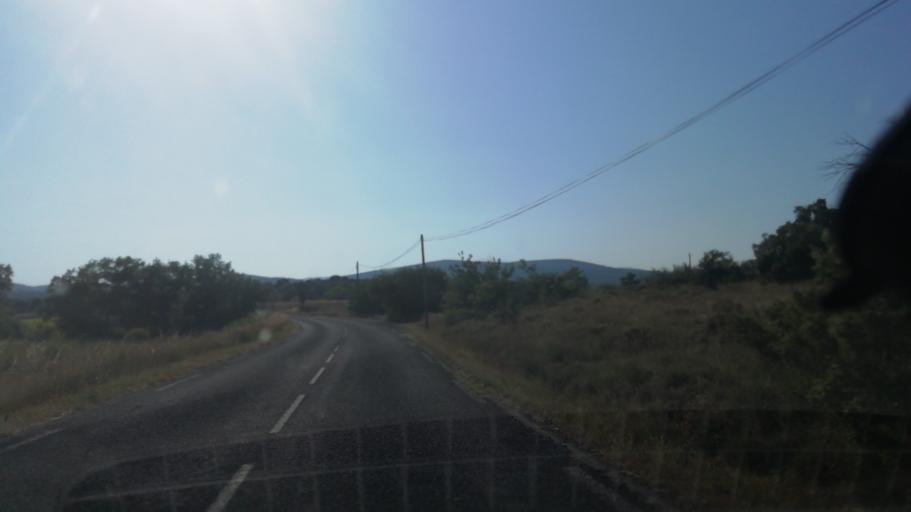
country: FR
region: Languedoc-Roussillon
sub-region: Departement de l'Herault
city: Saint-Martin-de-Londres
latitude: 43.8233
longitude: 3.7693
